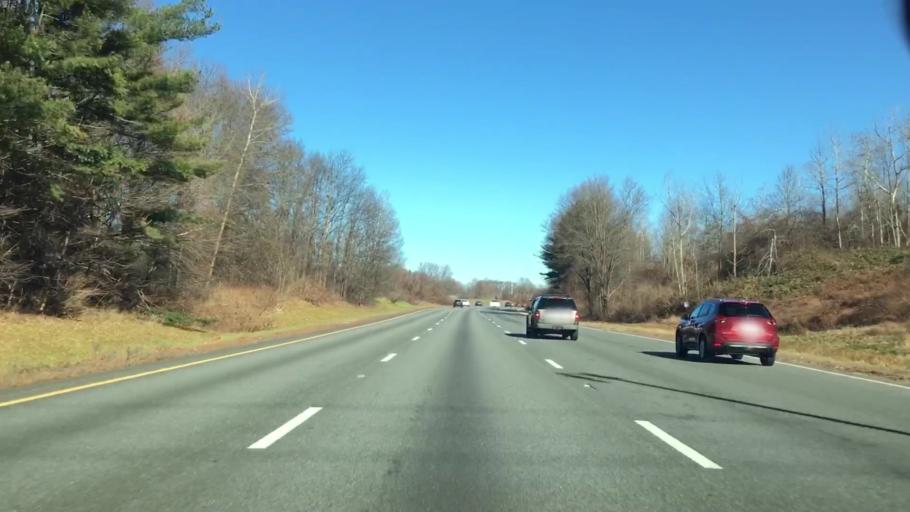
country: US
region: Massachusetts
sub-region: Essex County
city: Haverhill
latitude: 42.7835
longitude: -71.1145
